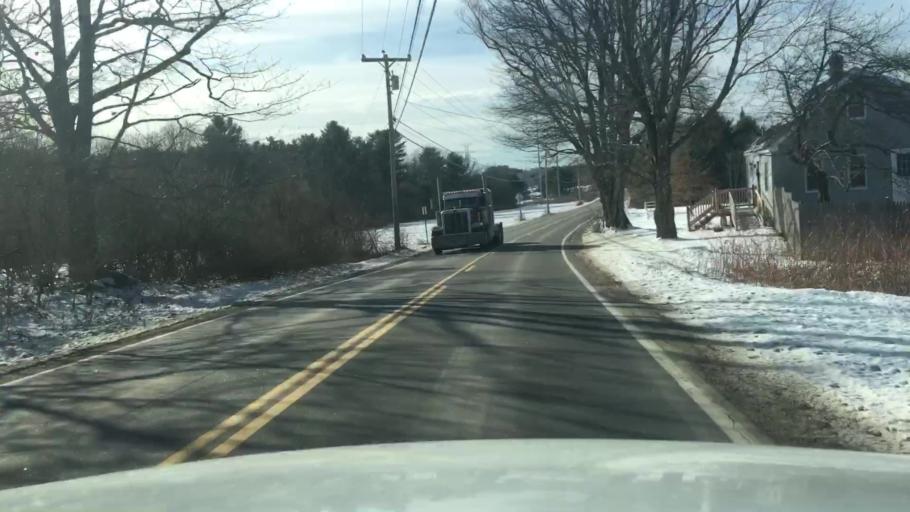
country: US
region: Maine
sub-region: Lincoln County
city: Wiscasset
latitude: 43.9724
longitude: -69.6918
